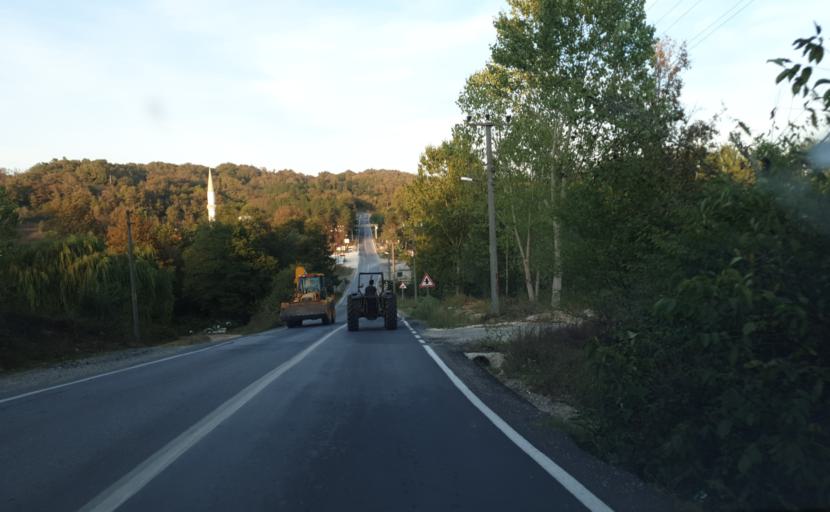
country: TR
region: Kirklareli
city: Sergen
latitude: 41.8336
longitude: 27.7896
